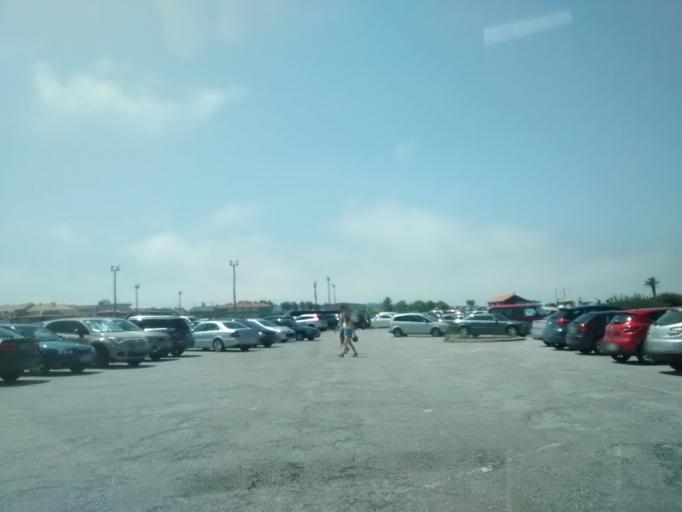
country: ES
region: Galicia
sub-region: Provincia de Pontevedra
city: O Grove
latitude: 42.4411
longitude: -8.8698
